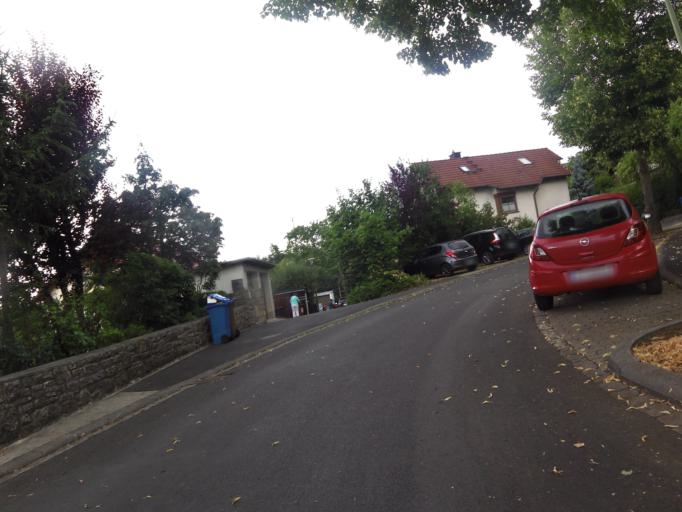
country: DE
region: Bavaria
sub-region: Regierungsbezirk Unterfranken
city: Wuerzburg
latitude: 49.8191
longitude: 9.9673
